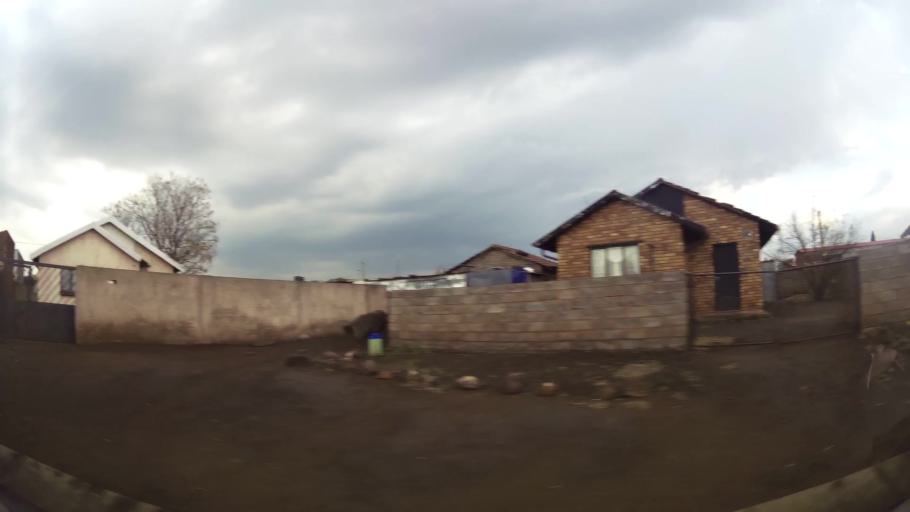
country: ZA
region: Gauteng
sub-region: Ekurhuleni Metropolitan Municipality
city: Germiston
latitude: -26.3688
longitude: 28.1325
